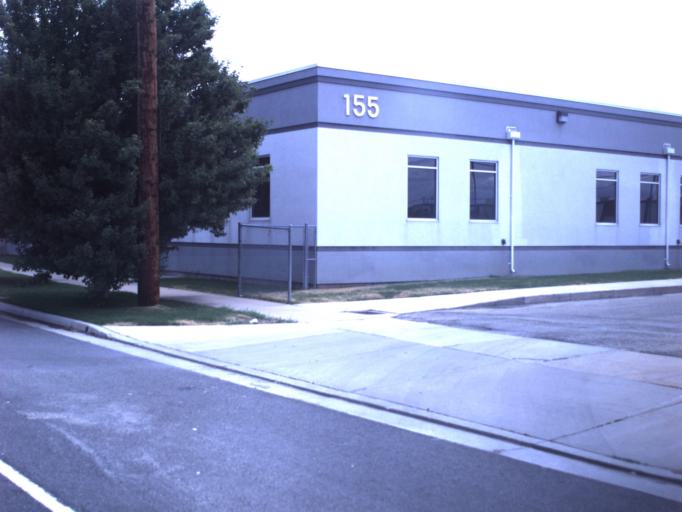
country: US
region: Utah
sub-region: Weber County
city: Ogden
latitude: 41.2082
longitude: -111.9780
